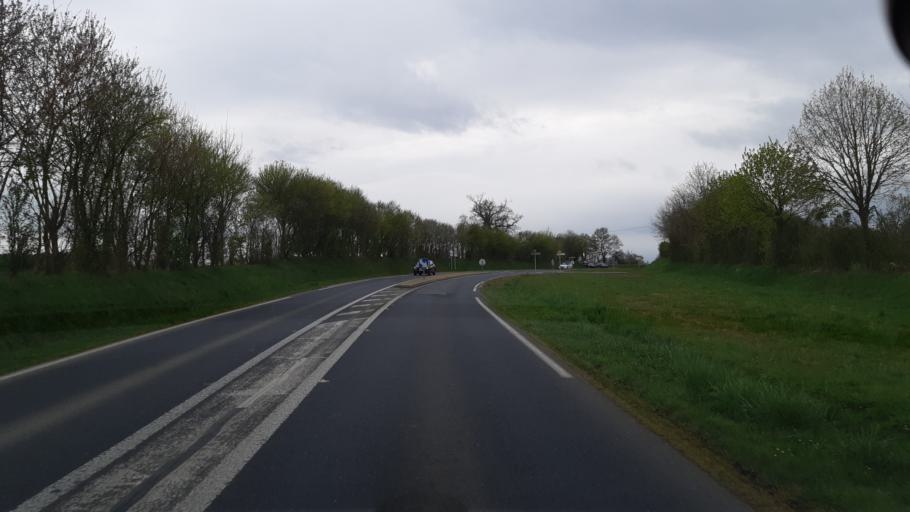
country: FR
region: Lower Normandy
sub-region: Departement de la Manche
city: Agneaux
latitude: 49.0328
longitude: -1.1354
